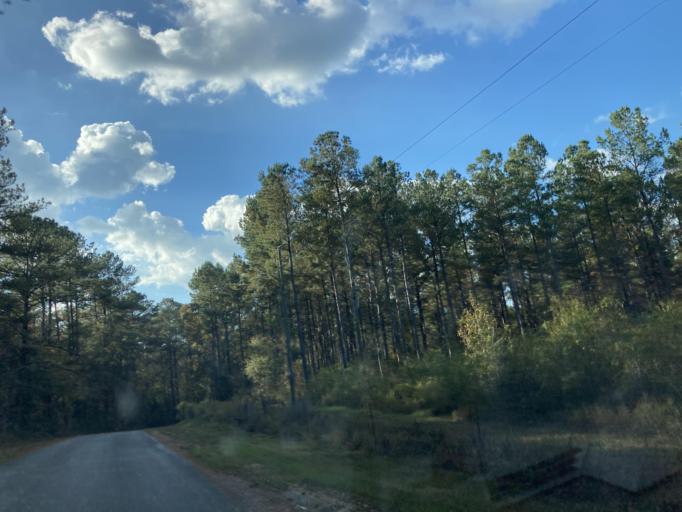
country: US
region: Mississippi
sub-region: Lamar County
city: Sumrall
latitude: 31.4452
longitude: -89.5842
